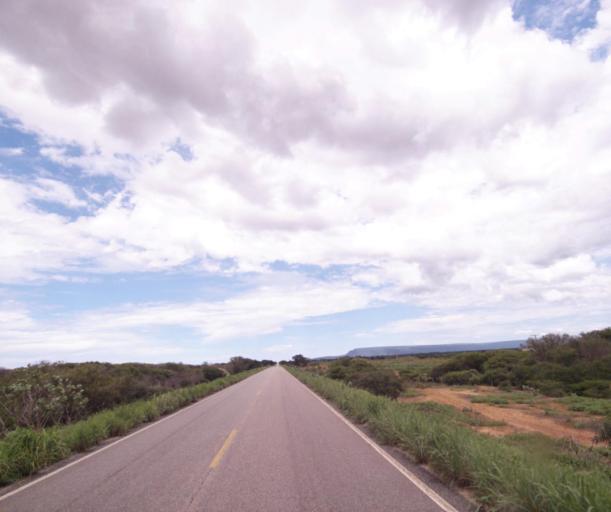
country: BR
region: Bahia
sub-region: Palmas De Monte Alto
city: Palmas de Monte Alto
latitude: -14.2585
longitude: -43.2729
